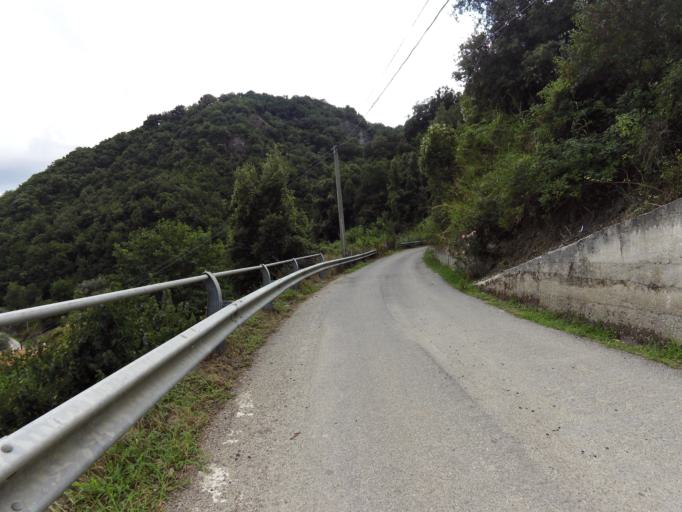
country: IT
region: Calabria
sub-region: Provincia di Reggio Calabria
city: Bivongi
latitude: 38.4853
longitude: 16.4289
